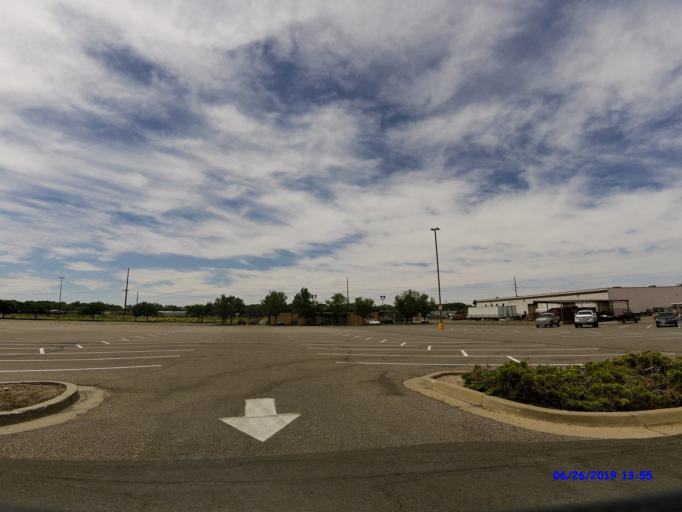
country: US
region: Utah
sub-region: Weber County
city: South Ogden
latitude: 41.1942
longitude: -111.9840
